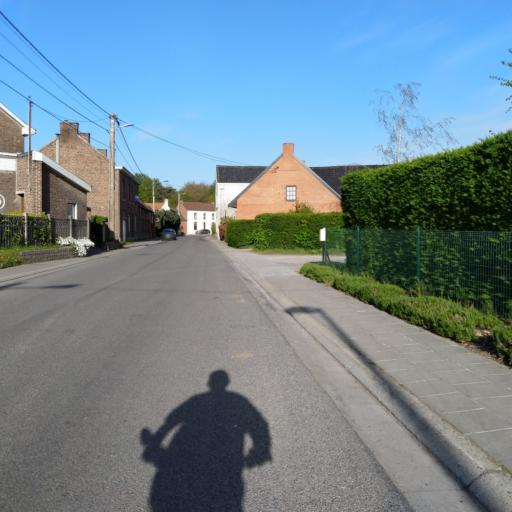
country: BE
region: Wallonia
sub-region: Province du Hainaut
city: Jurbise
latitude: 50.5066
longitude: 3.8851
